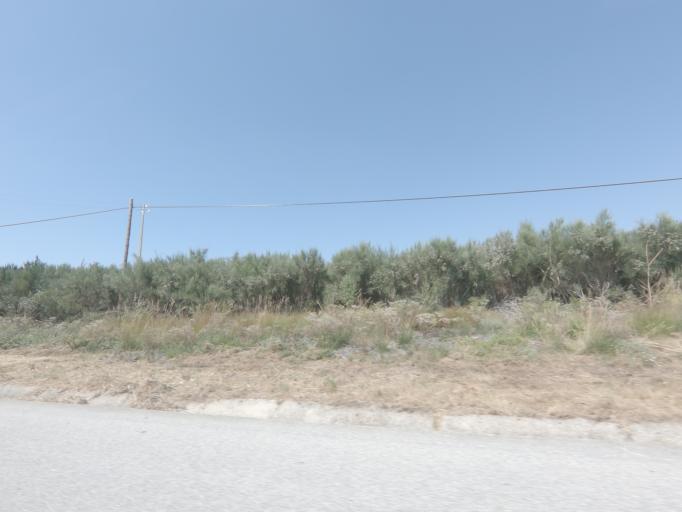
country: PT
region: Viseu
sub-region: Tarouca
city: Tarouca
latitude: 40.9865
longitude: -7.8037
